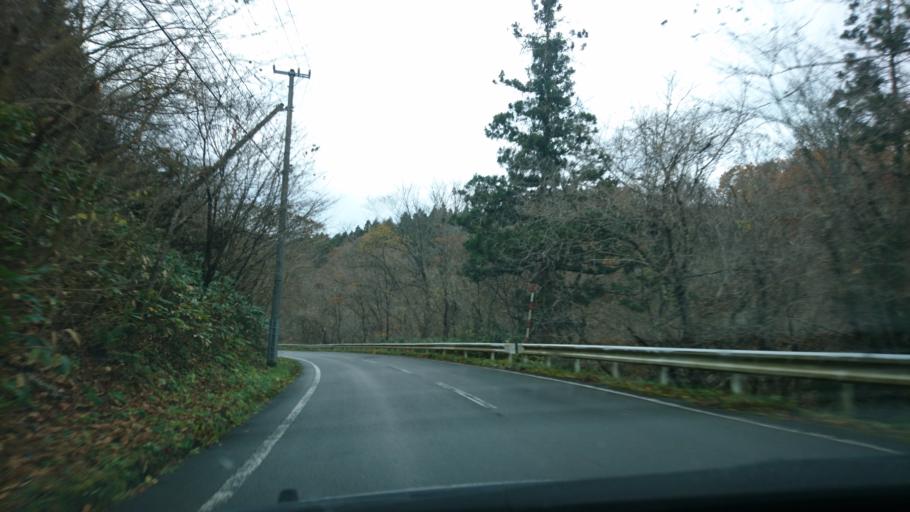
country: JP
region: Iwate
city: Ichinoseki
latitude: 38.9093
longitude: 140.8888
